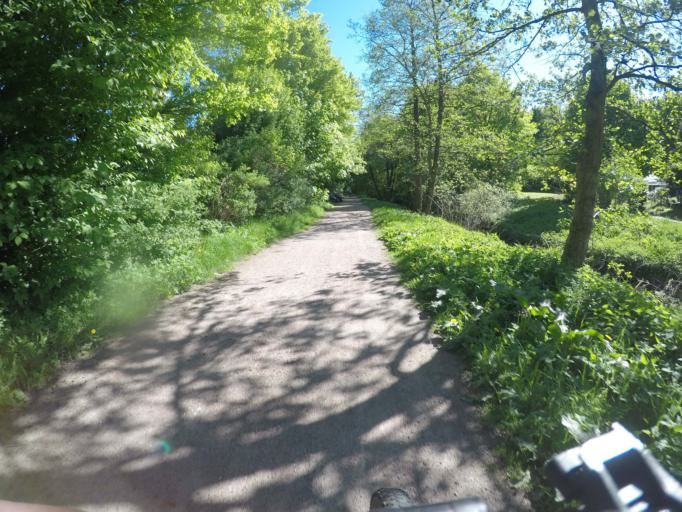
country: DE
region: Hamburg
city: Farmsen-Berne
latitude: 53.6080
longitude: 10.1237
